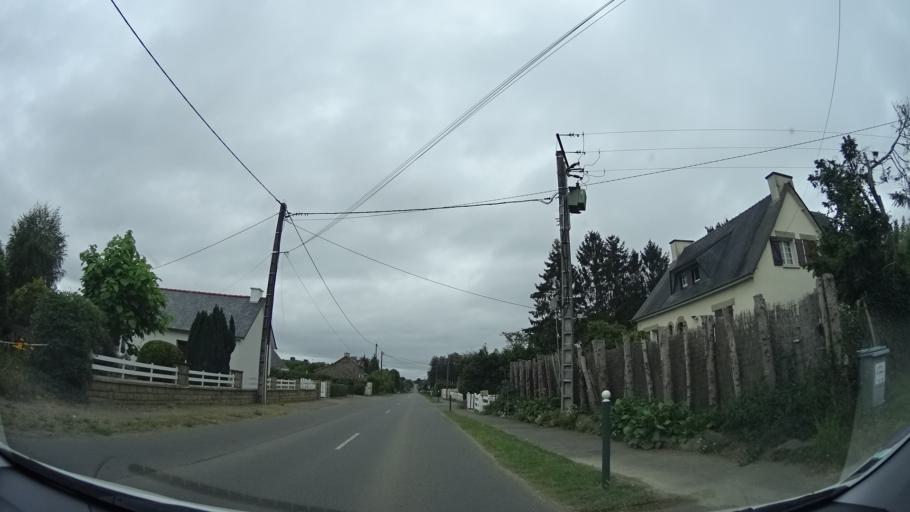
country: FR
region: Brittany
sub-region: Departement d'Ille-et-Vilaine
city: Saint-Domineuc
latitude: 48.3741
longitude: -1.8644
